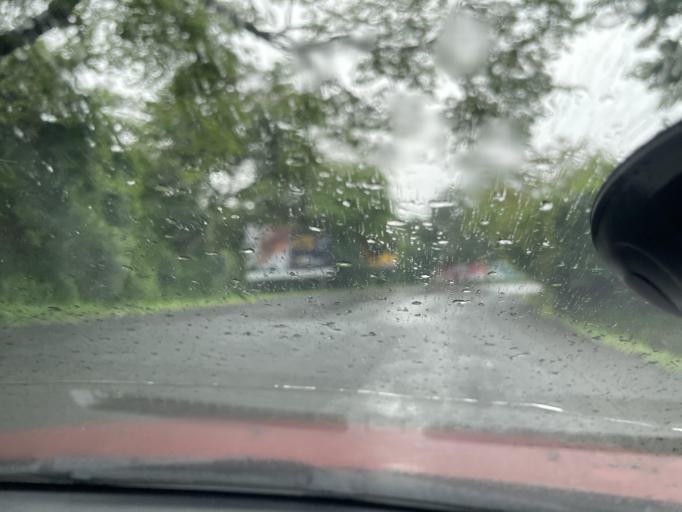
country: SV
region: La Union
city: Santa Rosa de Lima
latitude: 13.6076
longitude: -87.9098
